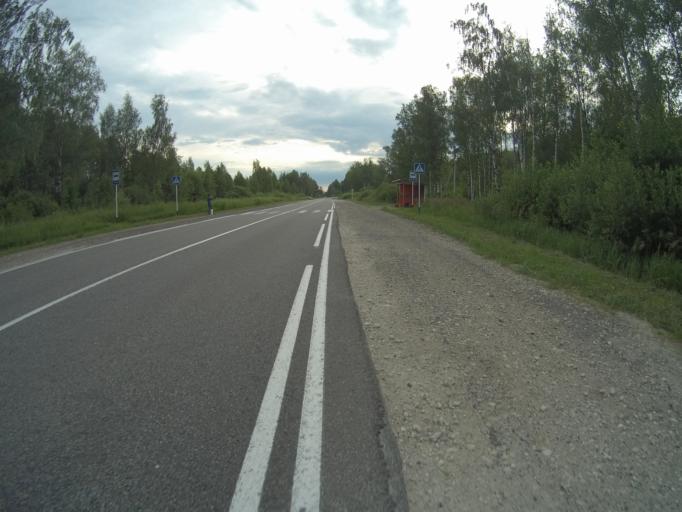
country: RU
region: Vladimir
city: Sudogda
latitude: 55.9765
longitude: 40.7506
